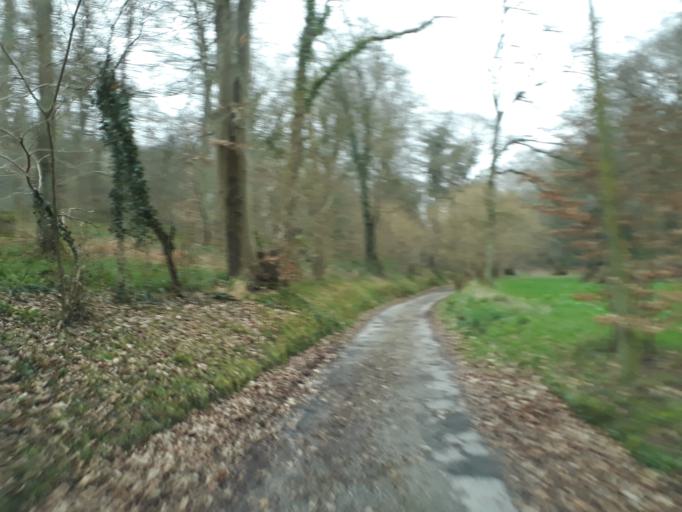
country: FR
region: Haute-Normandie
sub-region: Departement de la Seine-Maritime
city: Yport
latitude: 49.7293
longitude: 0.2962
